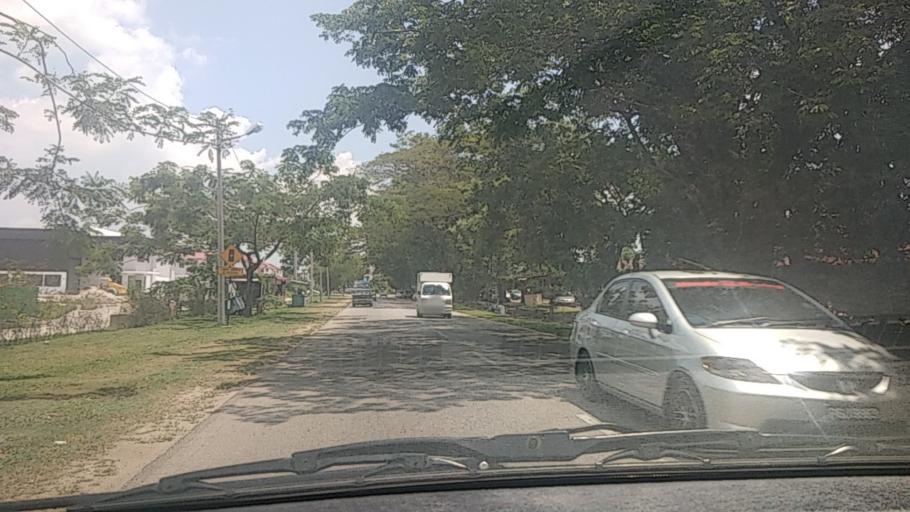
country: MY
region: Kedah
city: Sungai Petani
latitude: 5.6459
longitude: 100.5207
